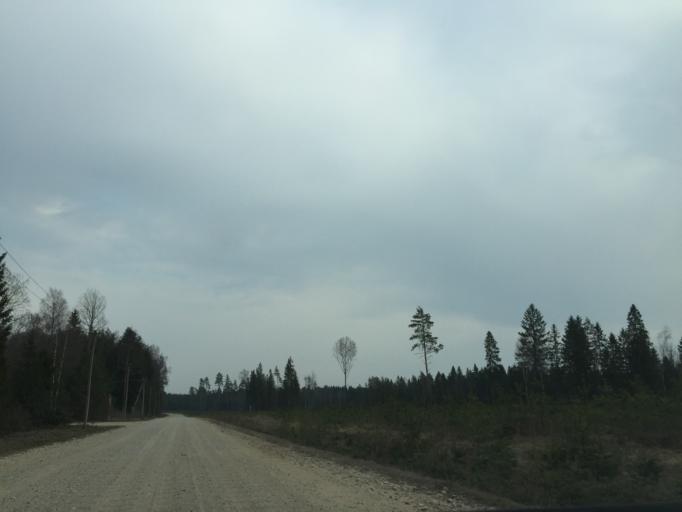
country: LV
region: Raunas
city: Rauna
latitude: 57.1599
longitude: 25.5324
